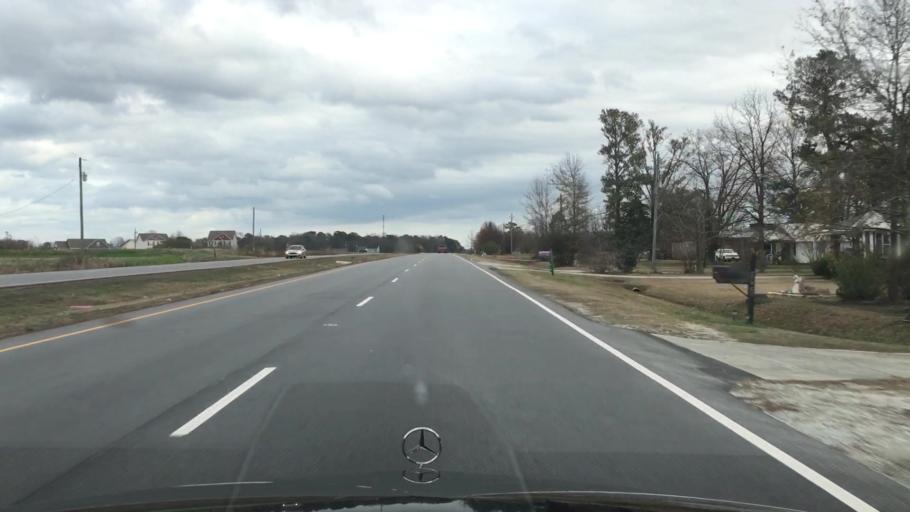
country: US
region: North Carolina
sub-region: Onslow County
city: Richlands
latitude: 34.9172
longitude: -77.6084
